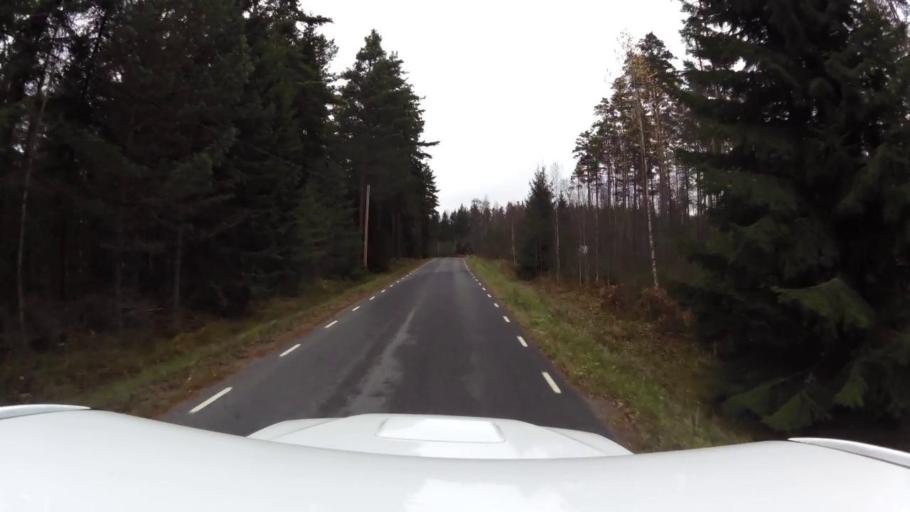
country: SE
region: OEstergoetland
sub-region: Kinda Kommun
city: Kisa
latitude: 58.1357
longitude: 15.4528
